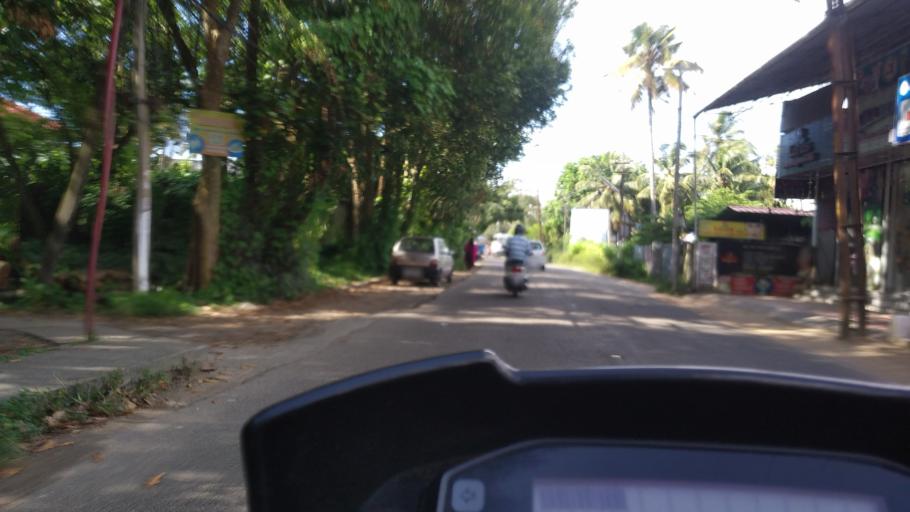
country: IN
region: Kerala
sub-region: Ernakulam
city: Elur
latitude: 10.0610
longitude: 76.2138
